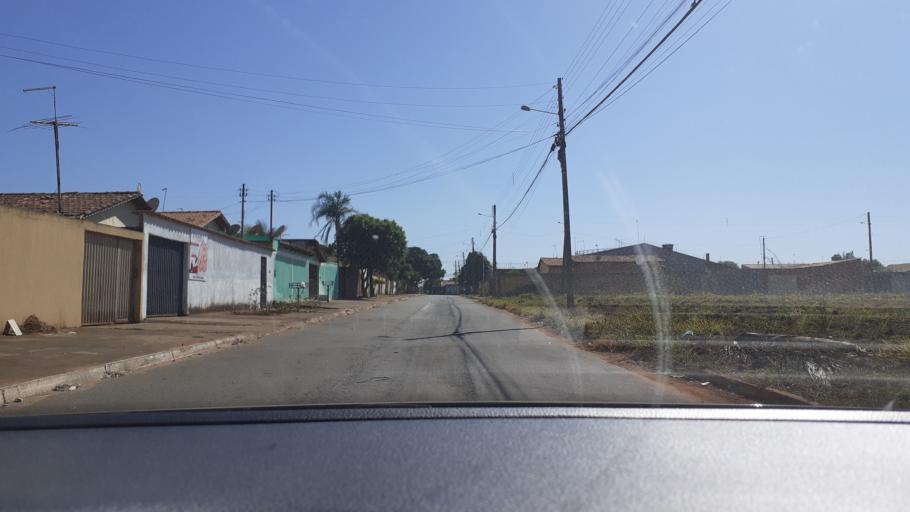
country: BR
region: Goias
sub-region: Aparecida De Goiania
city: Aparecida de Goiania
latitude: -16.8377
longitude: -49.2467
